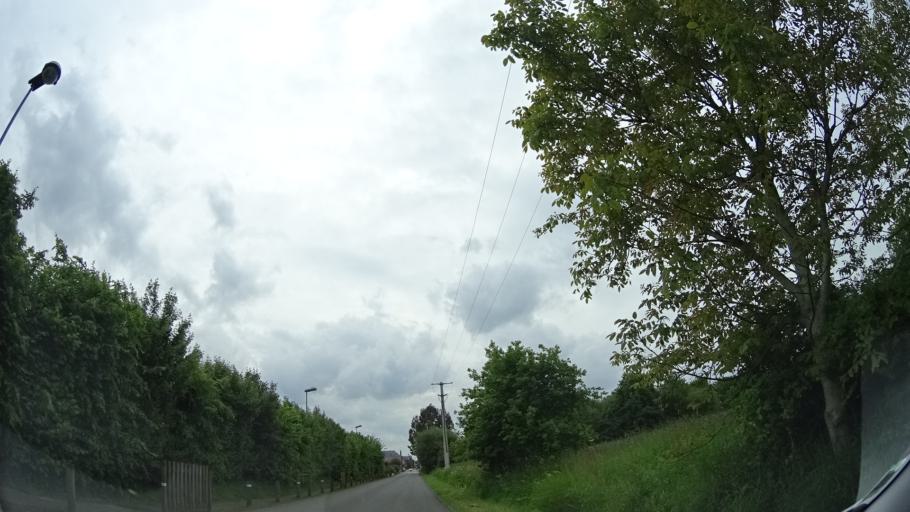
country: FR
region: Brittany
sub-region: Departement d'Ille-et-Vilaine
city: Tinteniac
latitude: 48.2742
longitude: -1.8530
